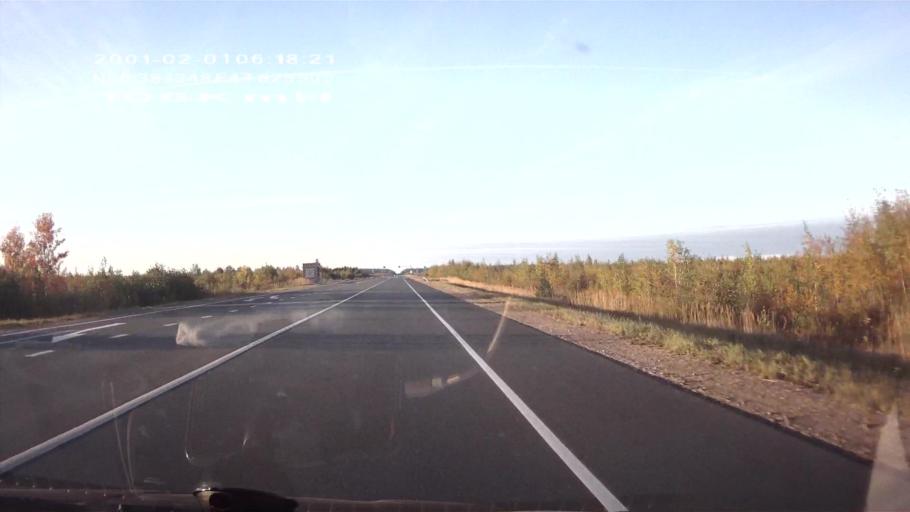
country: RU
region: Mariy-El
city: Medvedevo
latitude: 56.3838
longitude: 47.8255
